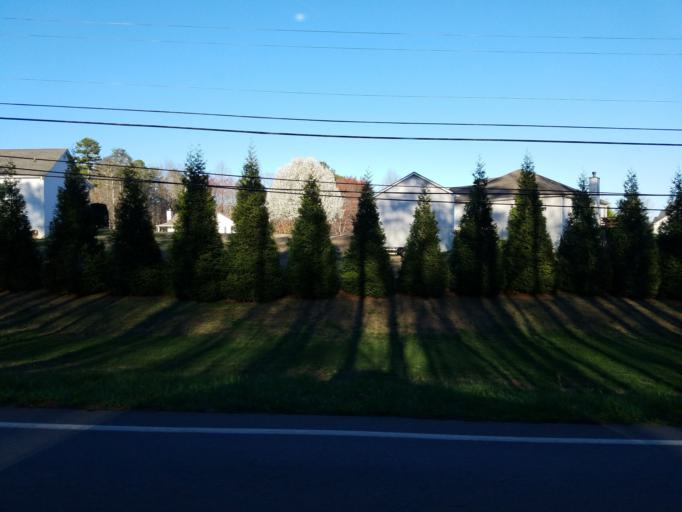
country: US
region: Georgia
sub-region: Pickens County
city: Jasper
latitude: 34.4274
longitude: -84.4203
